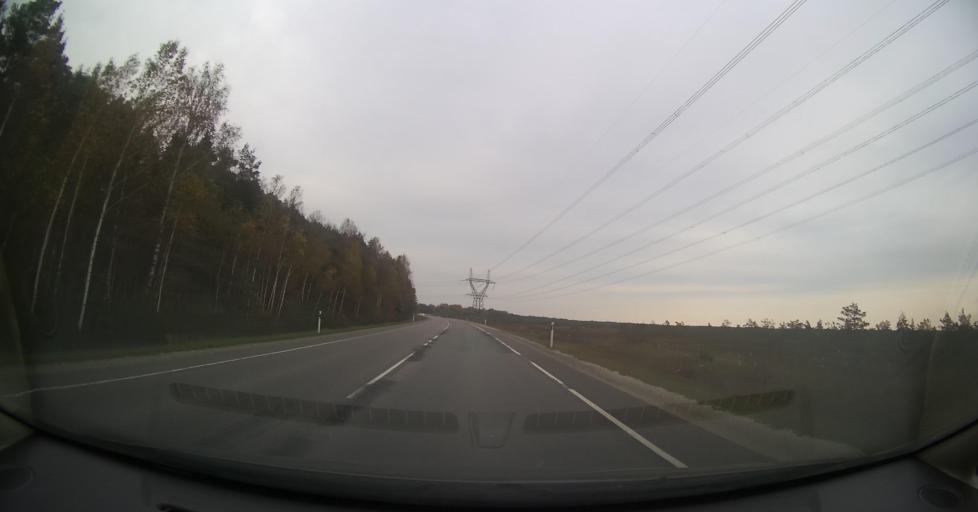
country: EE
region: Harju
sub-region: Nissi vald
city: Turba
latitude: 58.9944
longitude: 24.0626
